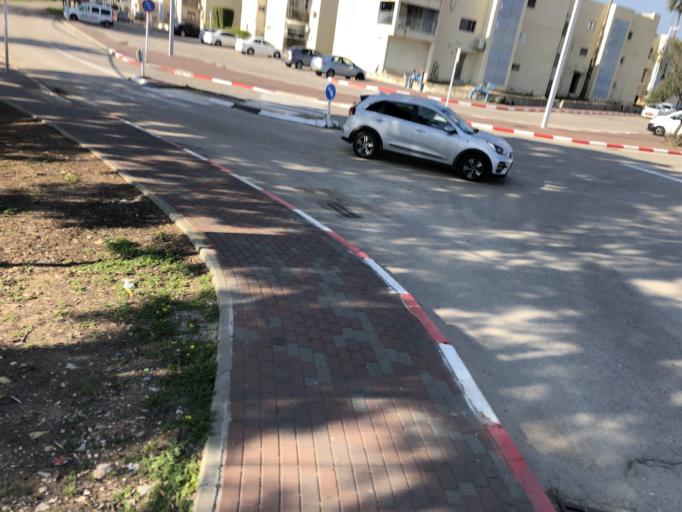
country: IL
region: Northern District
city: `Akko
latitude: 32.9172
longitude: 35.0922
